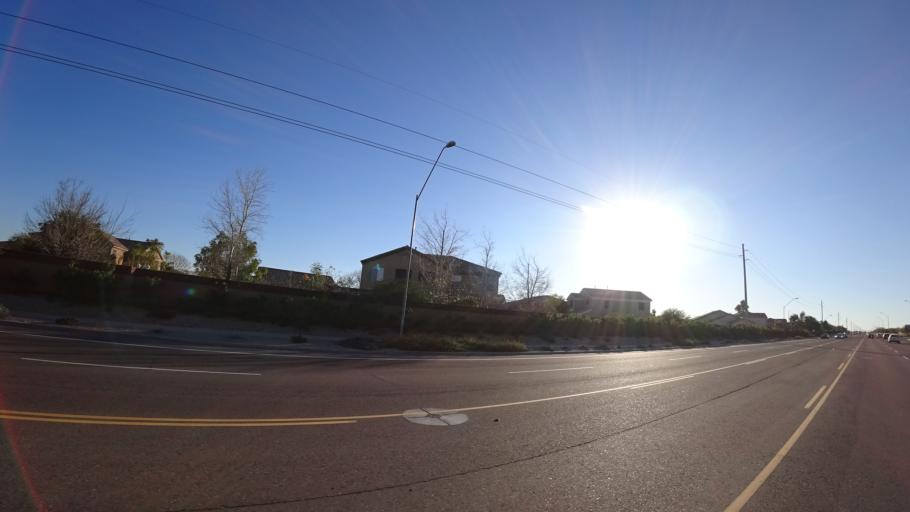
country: US
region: Arizona
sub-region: Maricopa County
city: Sun City
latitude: 33.6818
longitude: -112.2572
